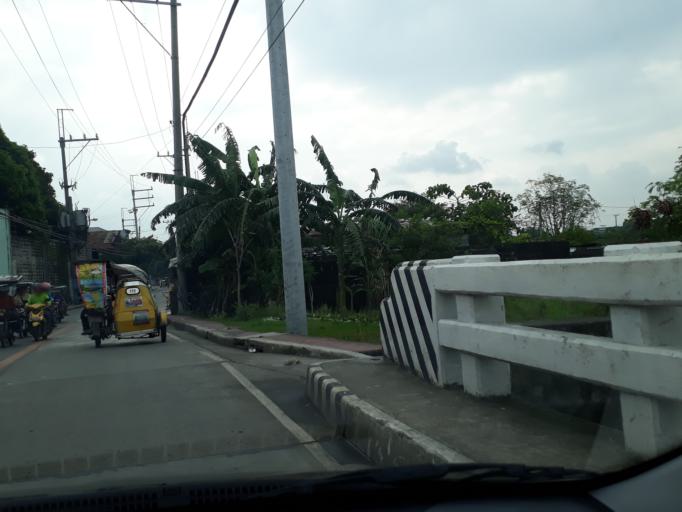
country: PH
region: Calabarzon
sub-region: Province of Rizal
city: Valenzuela
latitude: 14.7130
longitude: 120.9693
